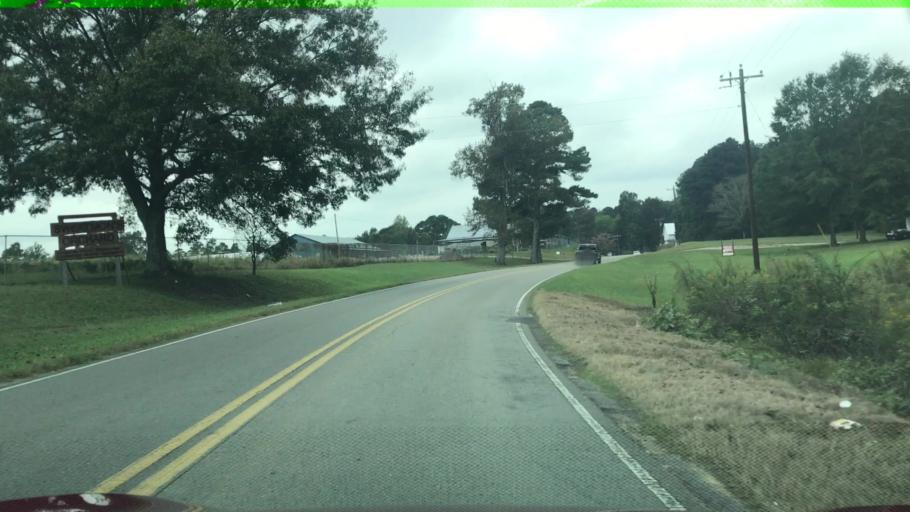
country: US
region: Alabama
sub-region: Cullman County
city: Good Hope
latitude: 34.0968
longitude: -87.0511
